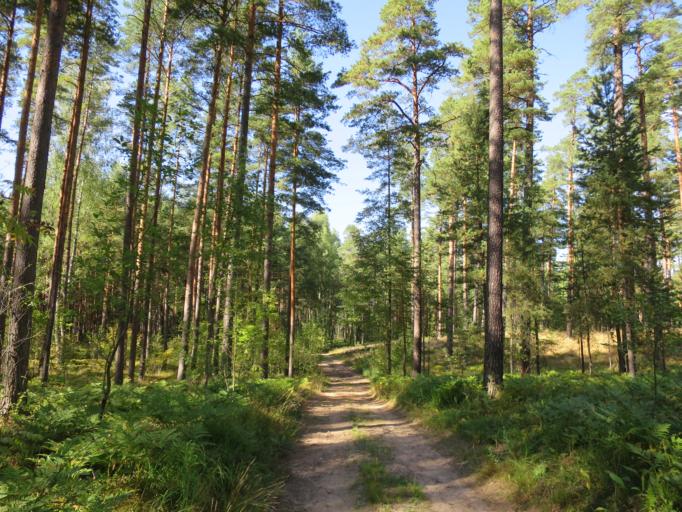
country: LV
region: Riga
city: Jaunciems
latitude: 57.0666
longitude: 24.2240
